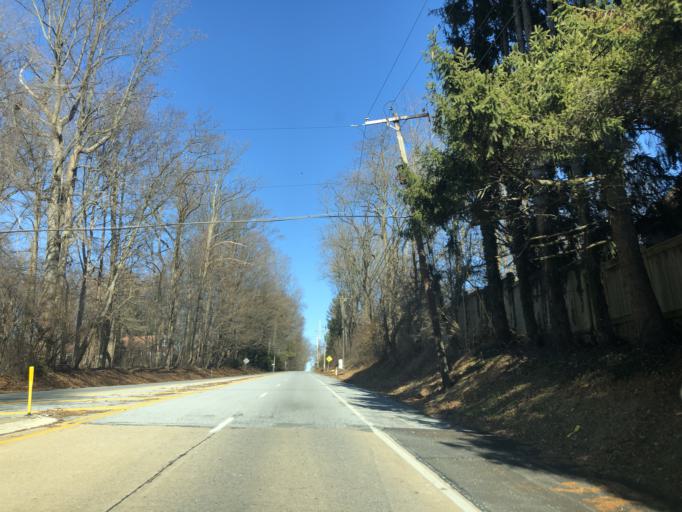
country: US
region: Pennsylvania
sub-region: Chester County
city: Kennett Square
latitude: 39.8581
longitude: -75.7158
